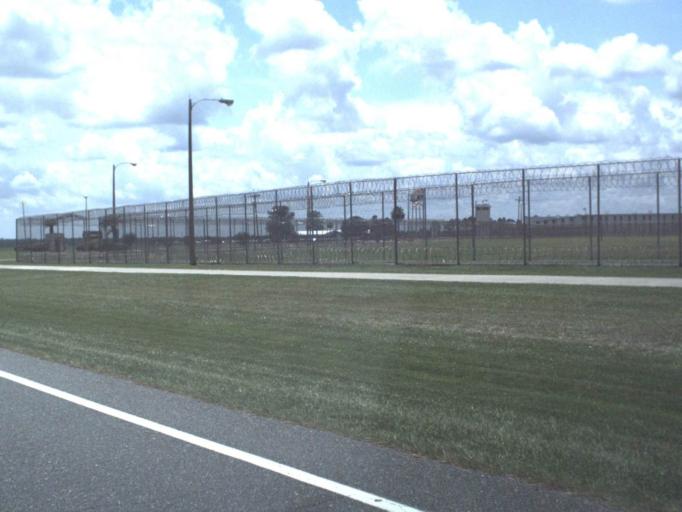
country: US
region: Florida
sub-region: Bradford County
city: Starke
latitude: 30.0637
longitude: -82.1819
